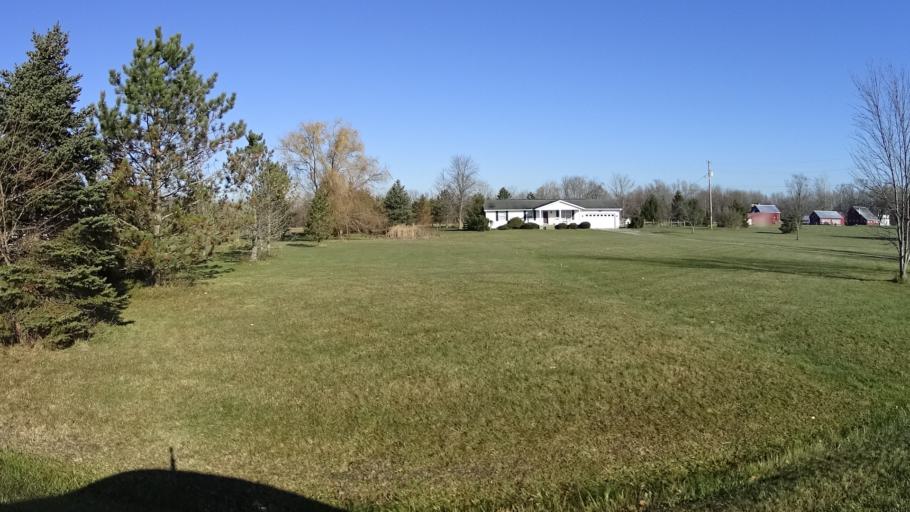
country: US
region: Ohio
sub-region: Lorain County
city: Wellington
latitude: 41.1368
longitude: -82.1257
